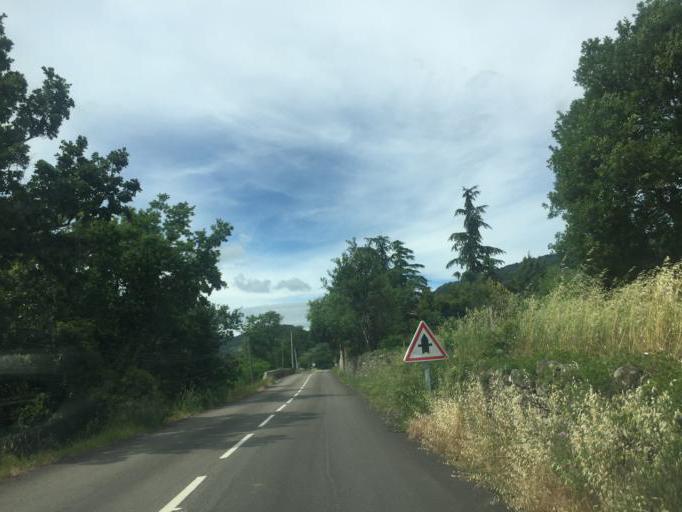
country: FR
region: Rhone-Alpes
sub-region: Departement de l'Ardeche
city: Villeneuve-de-Berg
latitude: 44.5941
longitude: 4.5360
